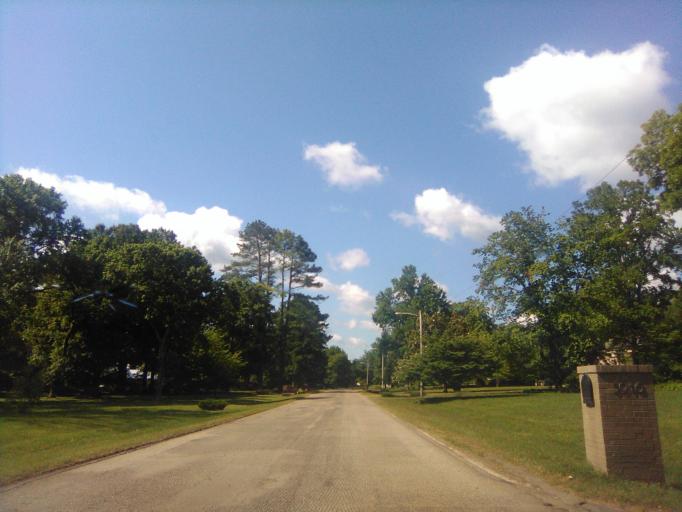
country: US
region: Tennessee
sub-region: Davidson County
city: Belle Meade
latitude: 36.1138
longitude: -86.8689
